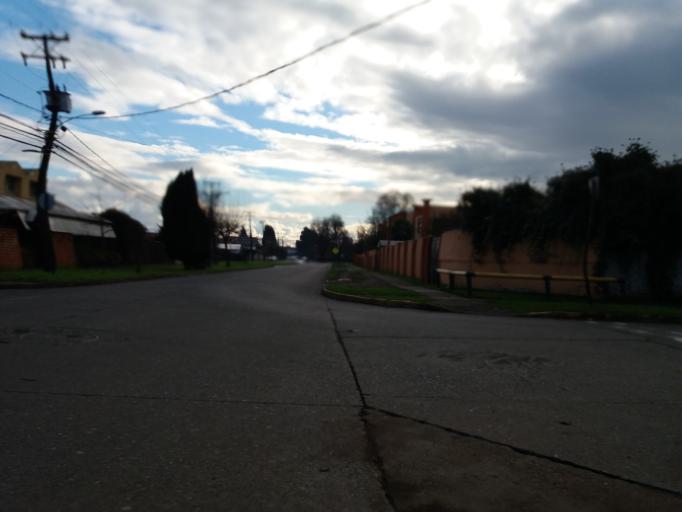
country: CL
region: Araucania
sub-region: Provincia de Cautin
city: Temuco
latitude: -38.7442
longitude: -72.6013
